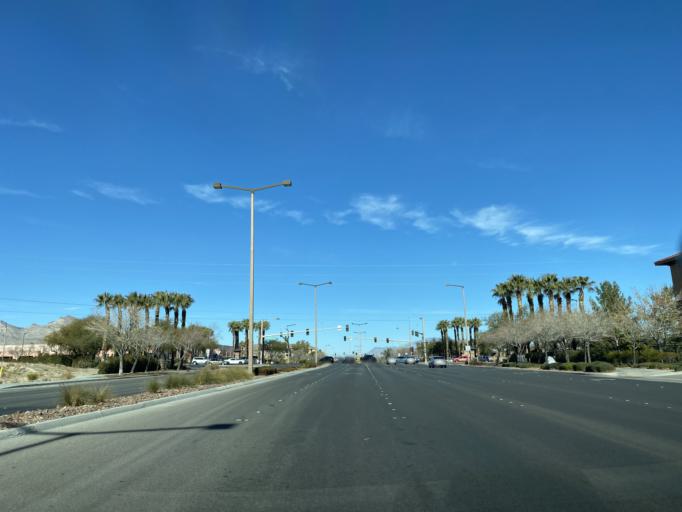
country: US
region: Nevada
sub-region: Clark County
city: Summerlin South
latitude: 36.1578
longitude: -115.3230
